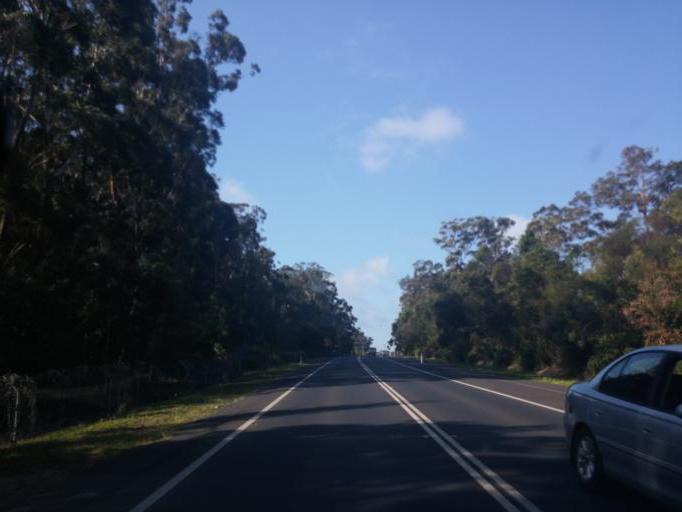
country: AU
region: New South Wales
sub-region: Coffs Harbour
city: Coffs Harbour
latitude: -30.2978
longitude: 153.1280
